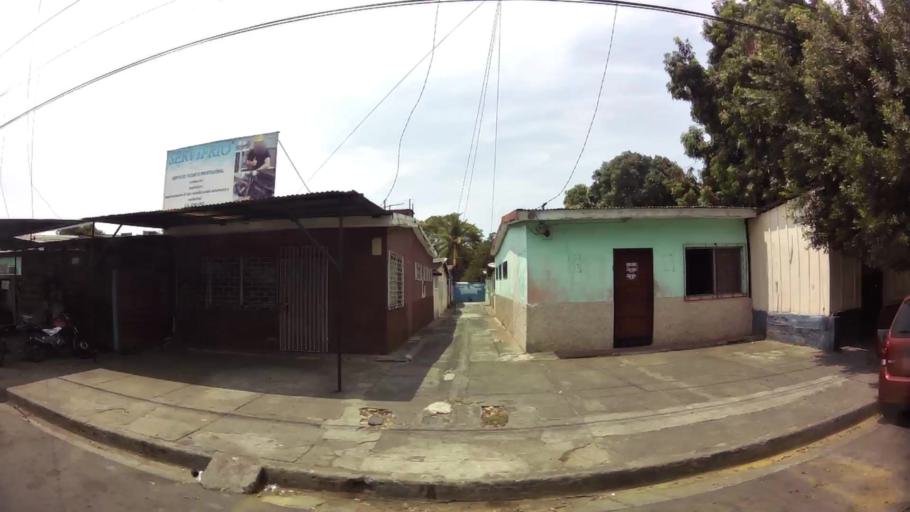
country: NI
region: Managua
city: Managua
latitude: 12.1488
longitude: -86.2893
